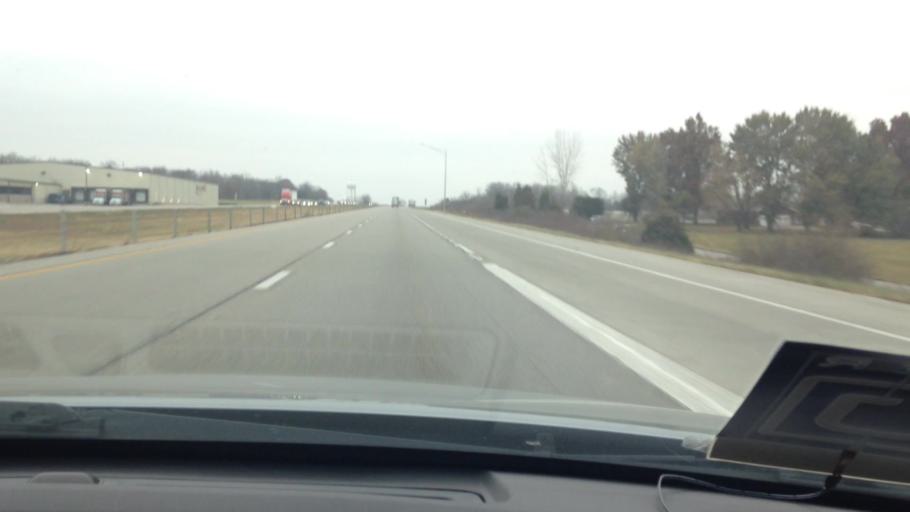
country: US
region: Missouri
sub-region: Cass County
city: Peculiar
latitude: 38.7416
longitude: -94.4723
